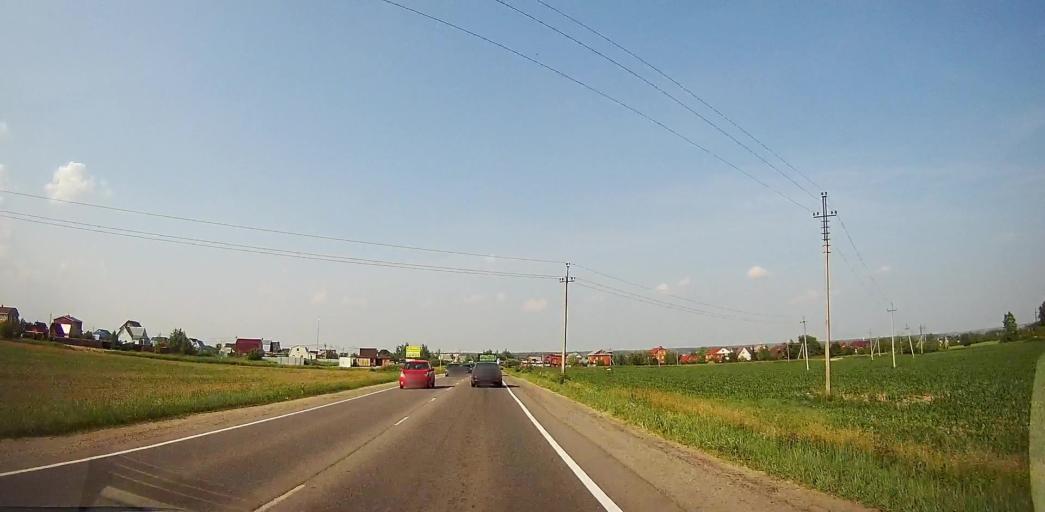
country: RU
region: Moskovskaya
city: Zhitnevo
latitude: 55.3354
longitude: 37.9076
